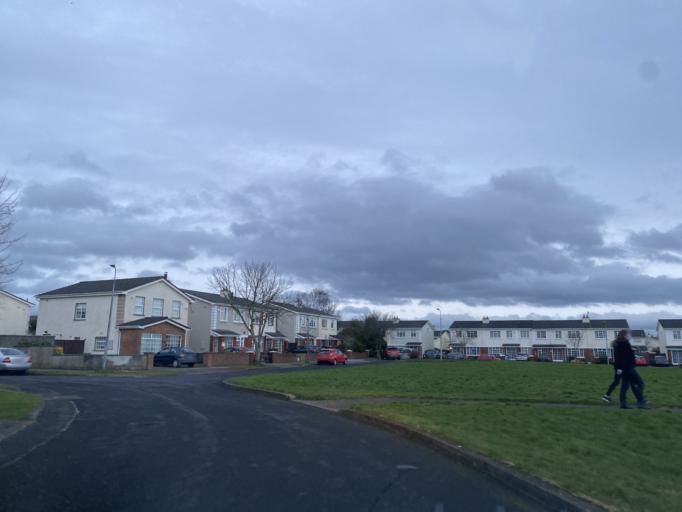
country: IE
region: Leinster
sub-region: Kildare
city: Celbridge
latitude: 53.3466
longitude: -6.5470
